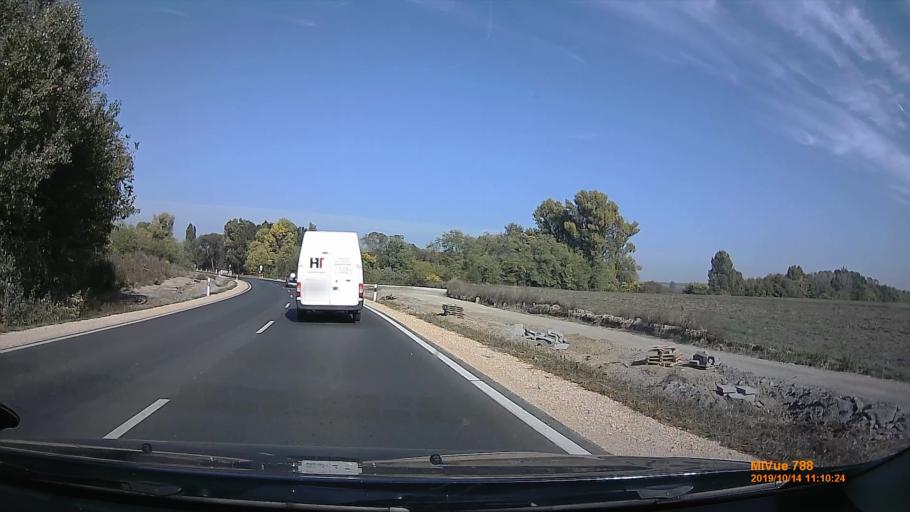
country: HU
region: Pest
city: Peteri
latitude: 47.3751
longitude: 19.4215
